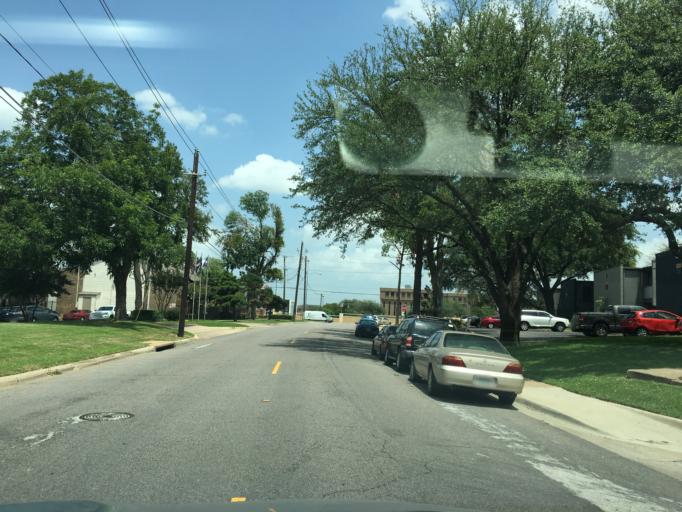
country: US
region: Texas
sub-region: Dallas County
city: University Park
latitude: 32.8962
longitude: -96.7709
